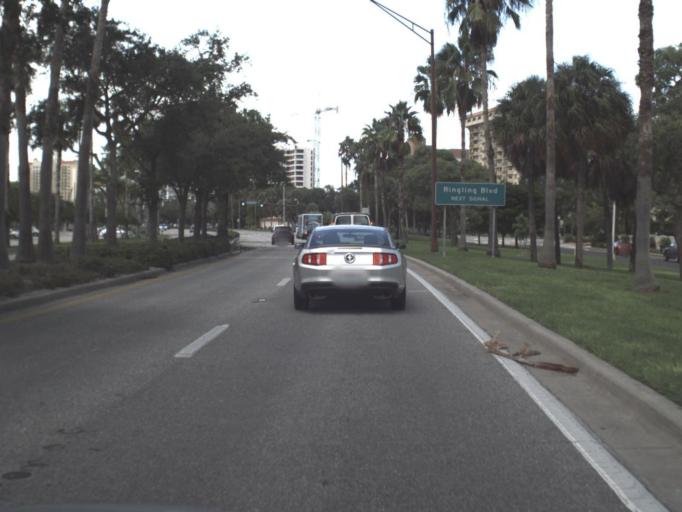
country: US
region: Florida
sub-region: Sarasota County
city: Sarasota
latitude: 27.3316
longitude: -82.5417
